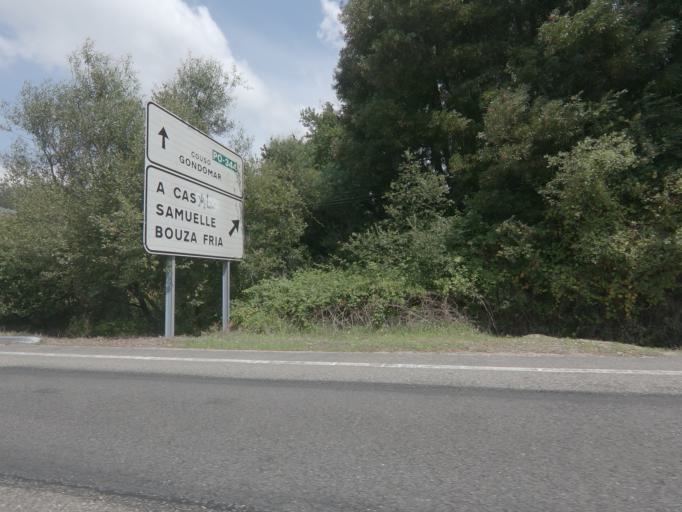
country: ES
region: Galicia
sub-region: Provincia de Pontevedra
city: Tomino
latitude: 42.0364
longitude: -8.7285
